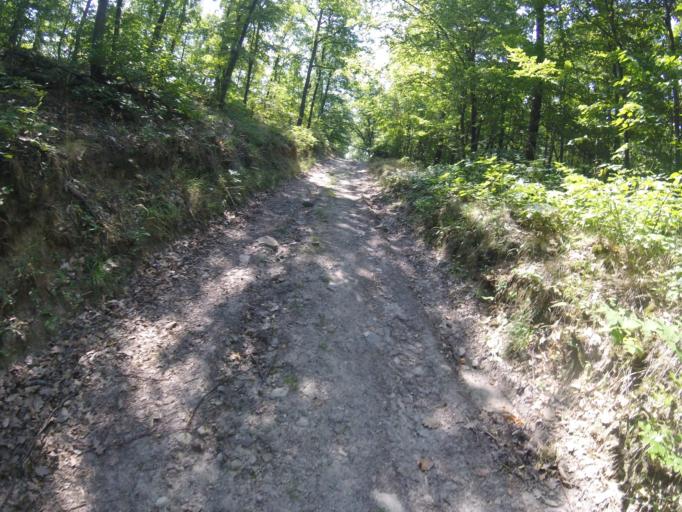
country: HU
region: Pest
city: Csobanka
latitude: 47.6831
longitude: 18.9597
